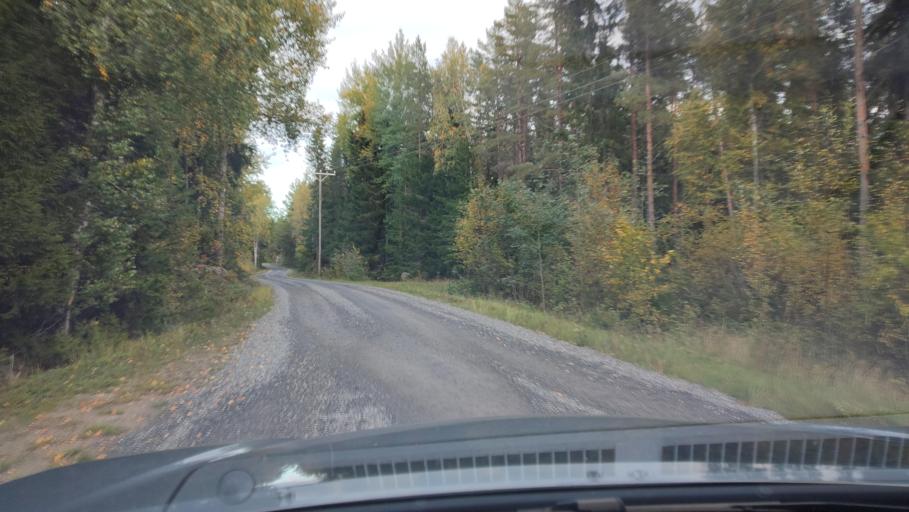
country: FI
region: Ostrobothnia
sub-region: Sydosterbotten
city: Kristinestad
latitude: 62.2301
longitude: 21.4215
